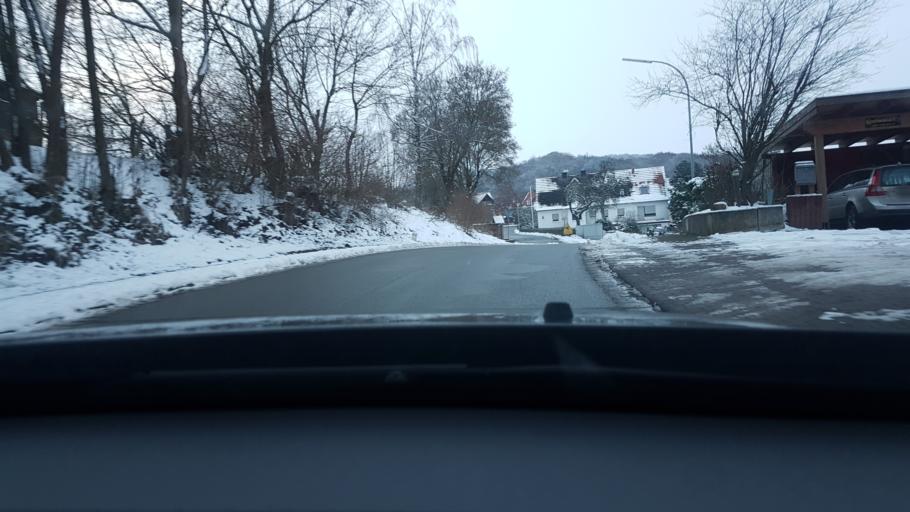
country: DE
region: Hesse
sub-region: Regierungsbezirk Kassel
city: Korbach
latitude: 51.3464
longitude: 8.8239
